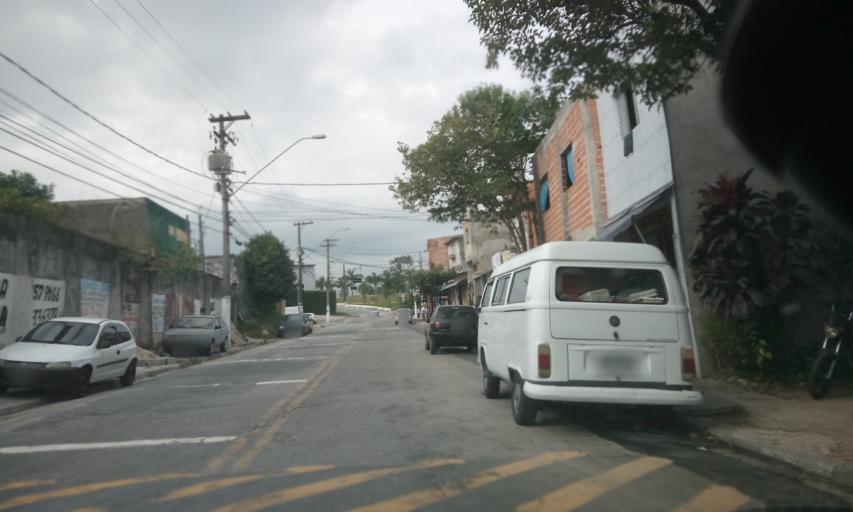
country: BR
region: Sao Paulo
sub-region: Sao Bernardo Do Campo
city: Sao Bernardo do Campo
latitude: -23.7717
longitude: -46.5995
